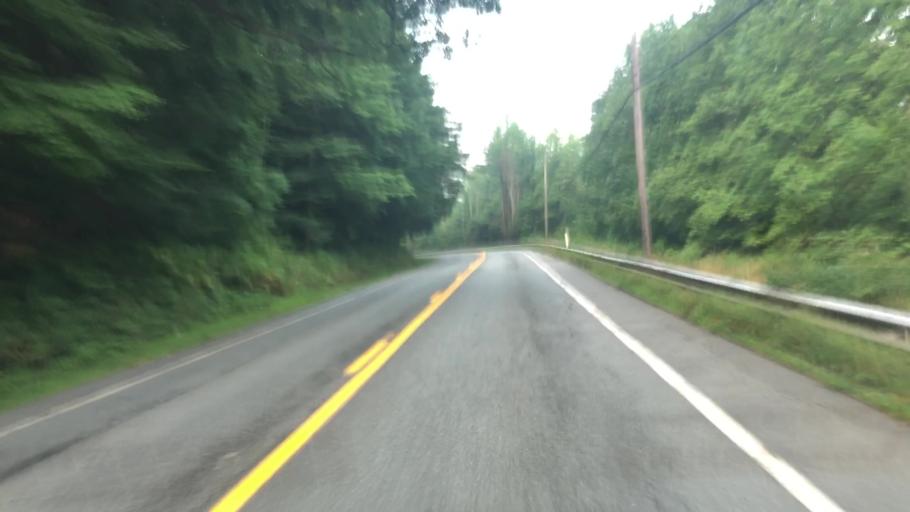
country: US
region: Massachusetts
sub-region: Franklin County
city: Buckland
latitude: 42.5818
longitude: -72.7982
